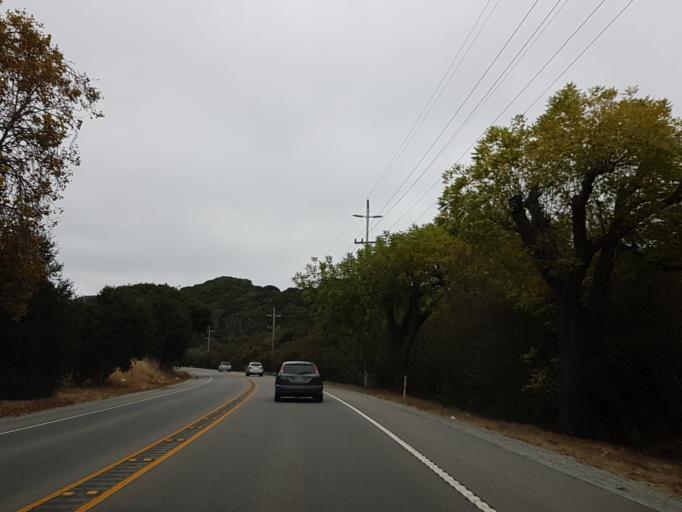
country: US
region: California
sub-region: Monterey County
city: Del Rey Oaks
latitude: 36.5744
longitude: -121.8211
